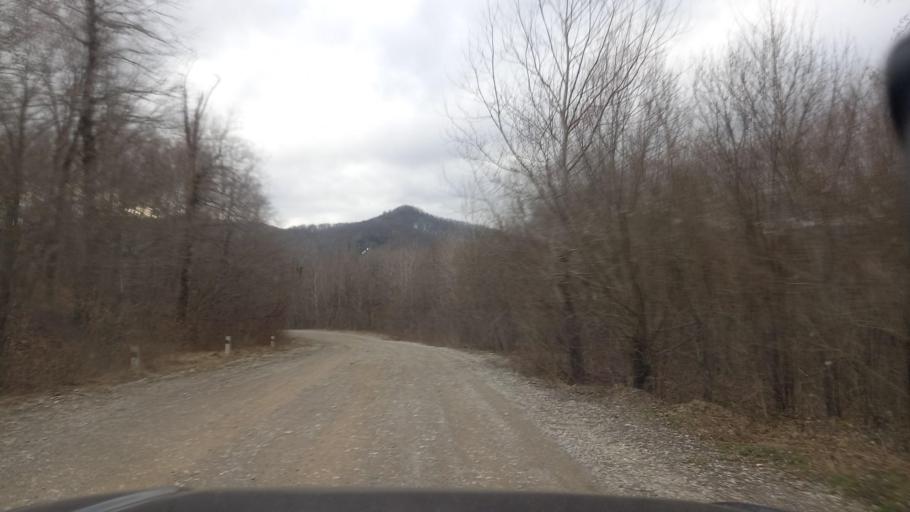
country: RU
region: Krasnodarskiy
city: Dzhubga
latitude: 44.5340
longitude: 38.7787
